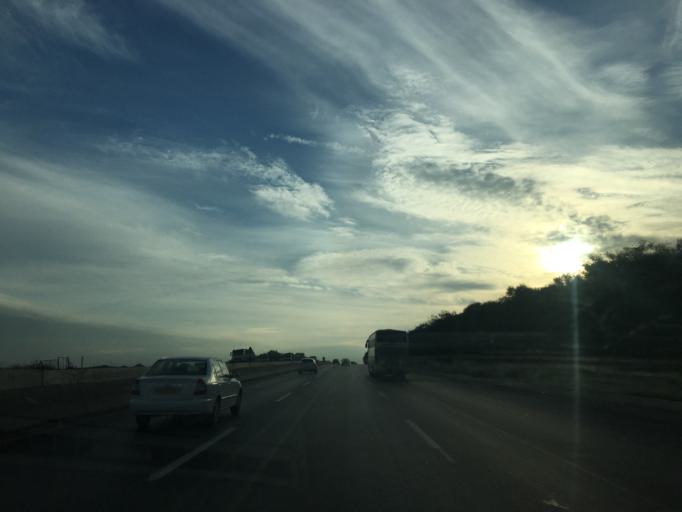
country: DZ
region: Bouira
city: Draa el Mizan
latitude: 36.4738
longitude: 3.7561
